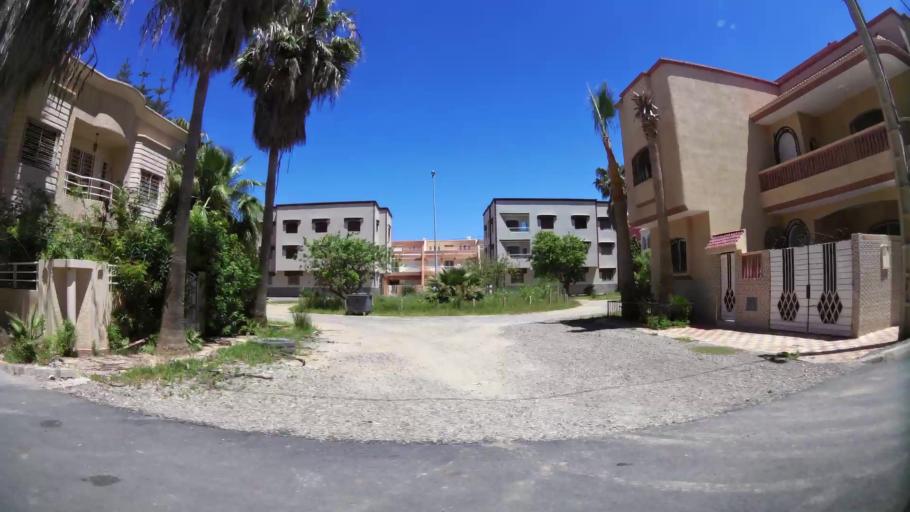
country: MA
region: Oriental
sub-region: Berkane-Taourirt
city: Madagh
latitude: 35.0827
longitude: -2.2369
